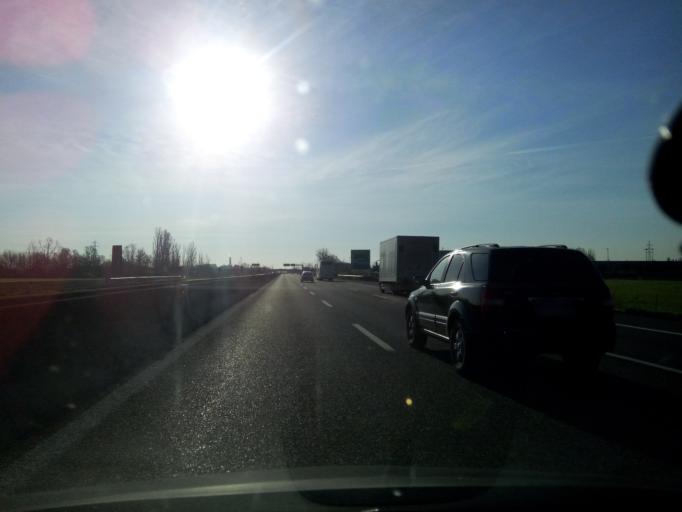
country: IT
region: Emilia-Romagna
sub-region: Provincia di Parma
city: Baganzola
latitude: 44.8435
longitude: 10.3238
